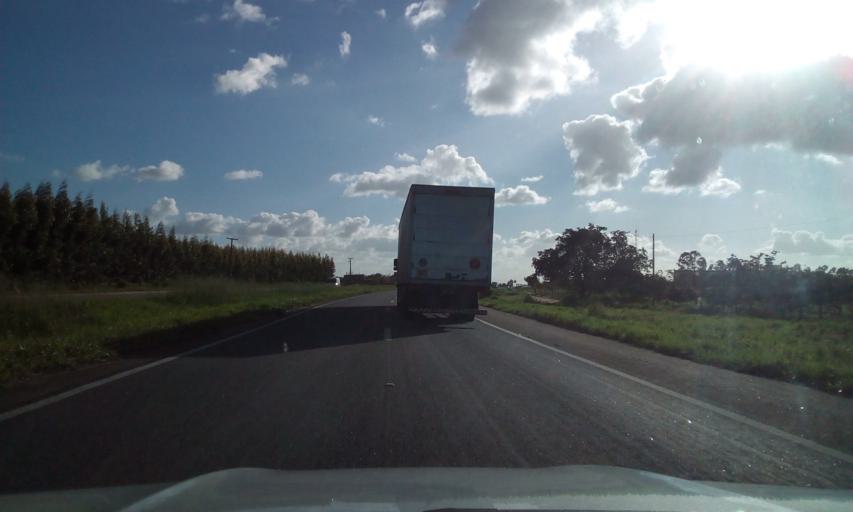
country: BR
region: Paraiba
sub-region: Cruz Do Espirito Santo
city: Cruz do Espirito Santo
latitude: -7.2055
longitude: -35.1459
